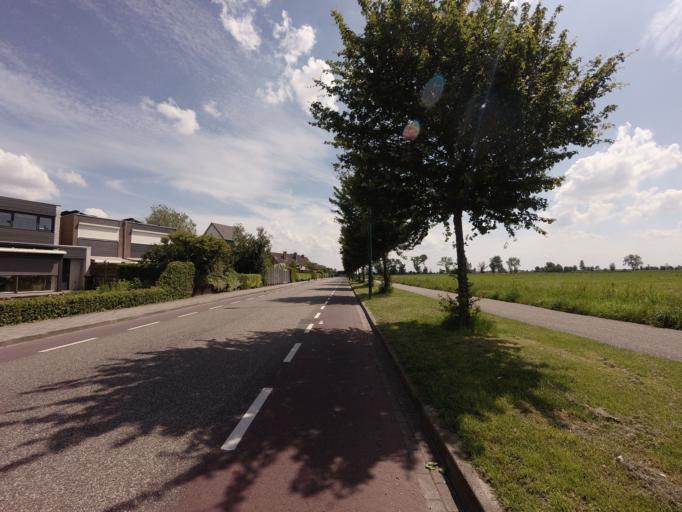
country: NL
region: Utrecht
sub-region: Gemeente Montfoort
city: Montfoort
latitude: 52.0389
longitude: 4.9477
